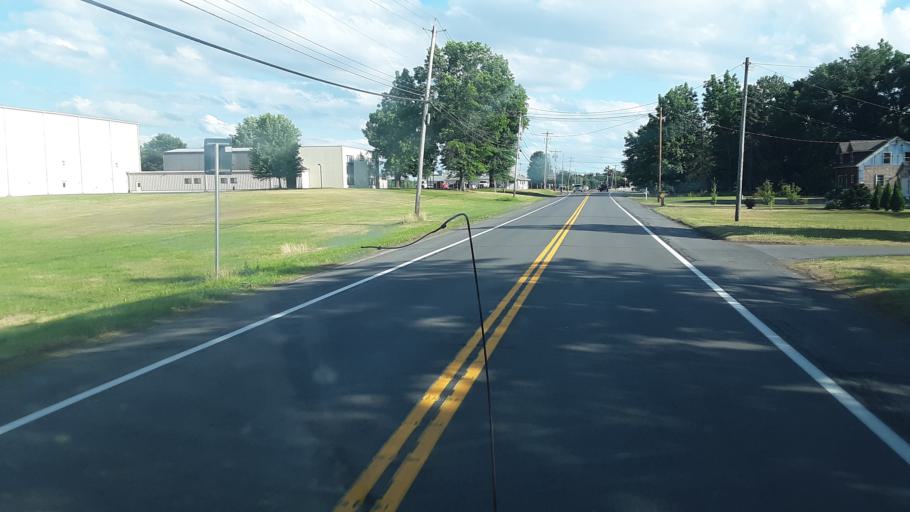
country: US
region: New York
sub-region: Oneida County
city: Rome
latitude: 43.2868
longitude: -75.4713
